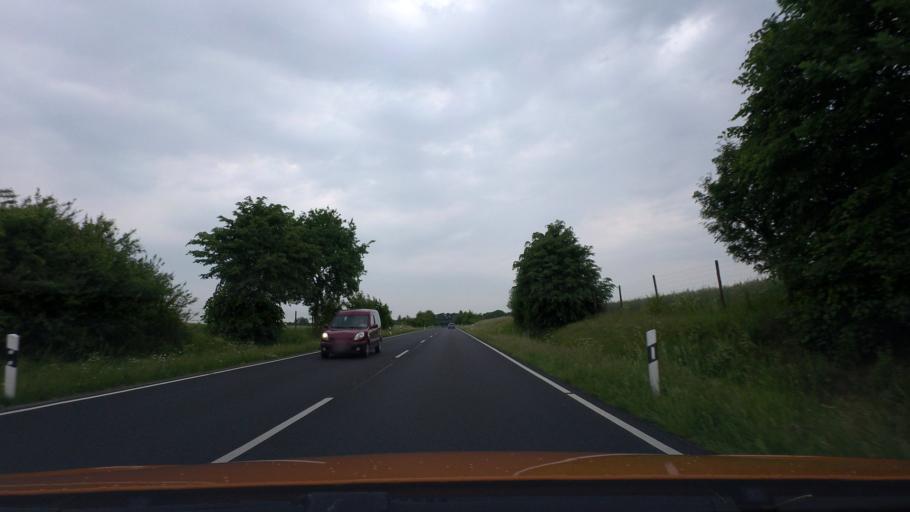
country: DE
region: Lower Saxony
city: Wietzen
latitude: 52.6689
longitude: 9.1041
